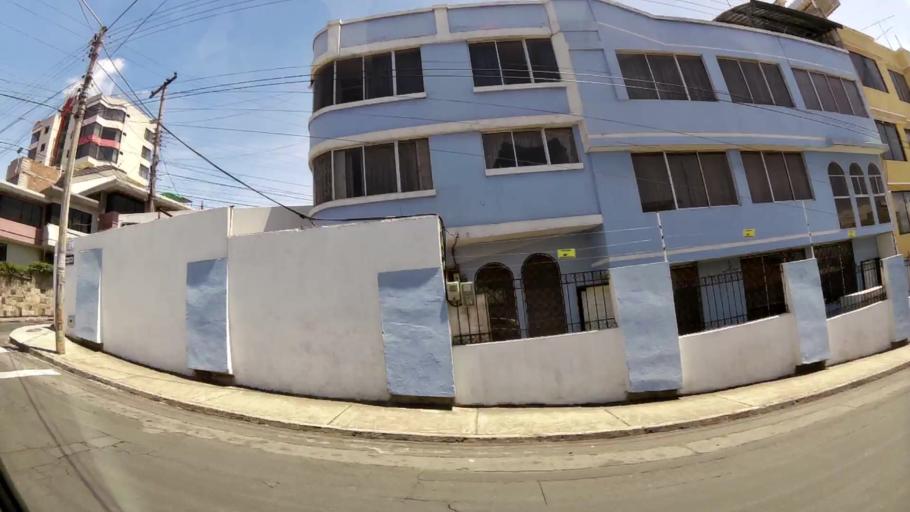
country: EC
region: Chimborazo
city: Riobamba
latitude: -1.6634
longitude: -78.6573
